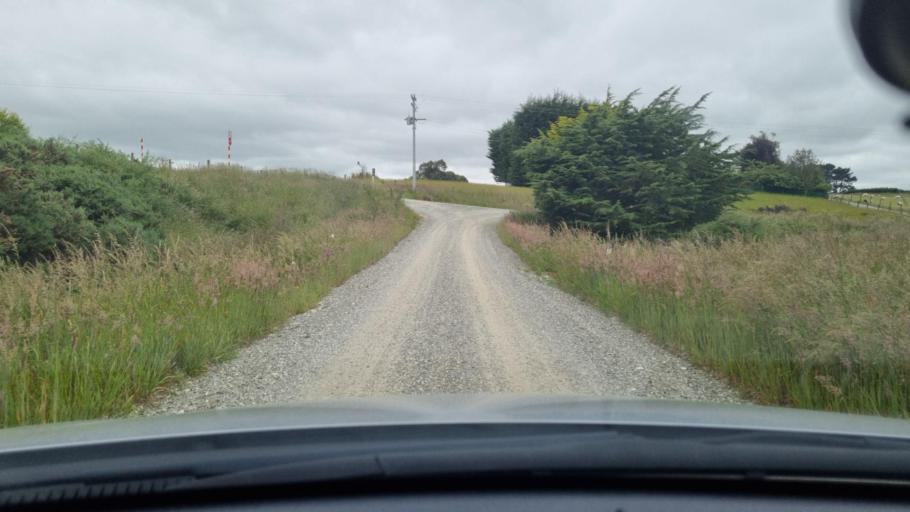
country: NZ
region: Southland
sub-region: Invercargill City
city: Invercargill
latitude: -46.3228
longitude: 168.3406
